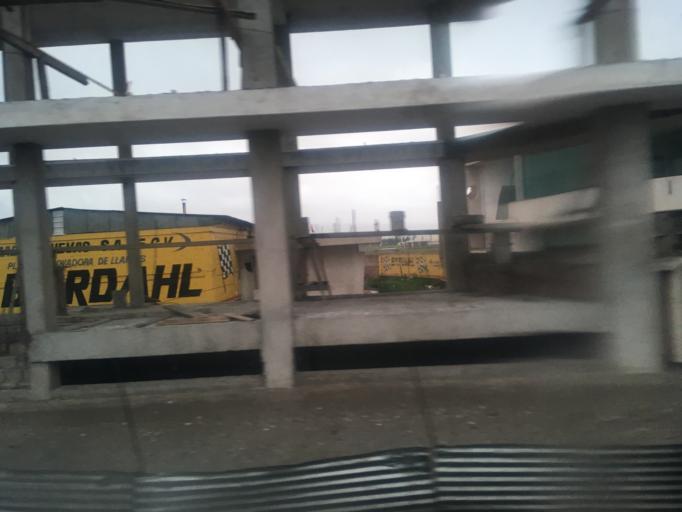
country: MX
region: Puebla
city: Chignahuapan
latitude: 19.8486
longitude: -98.0266
